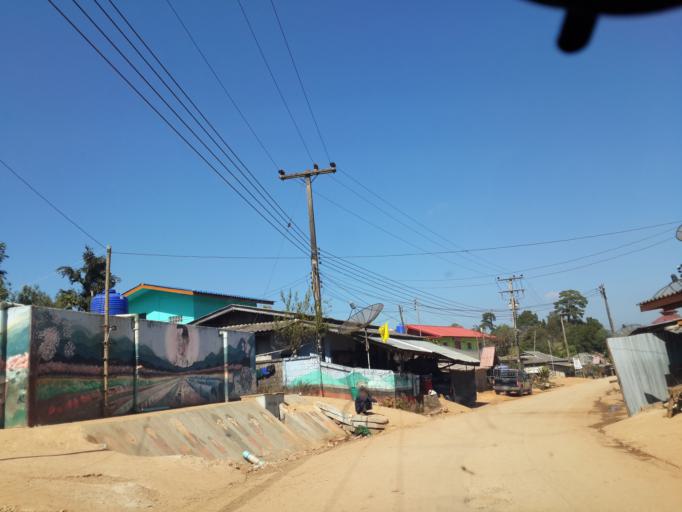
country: TH
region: Chiang Mai
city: Fang
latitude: 19.9368
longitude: 99.0411
